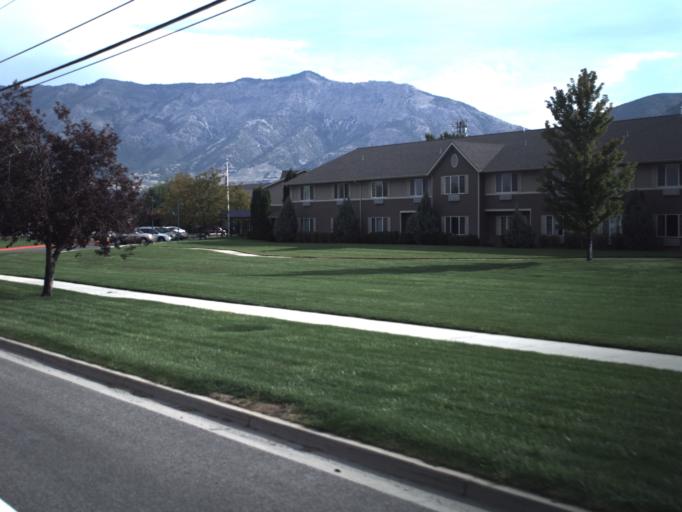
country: US
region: Utah
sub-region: Weber County
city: Harrisville
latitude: 41.2810
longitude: -111.9691
